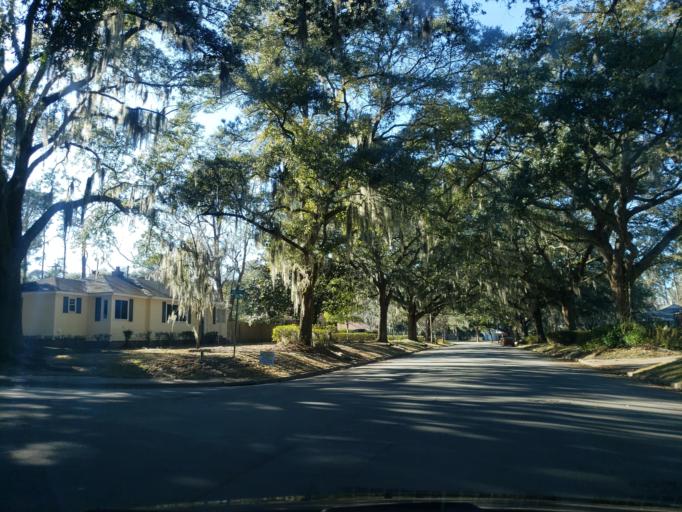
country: US
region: Georgia
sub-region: Chatham County
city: Thunderbolt
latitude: 32.0251
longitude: -81.1008
